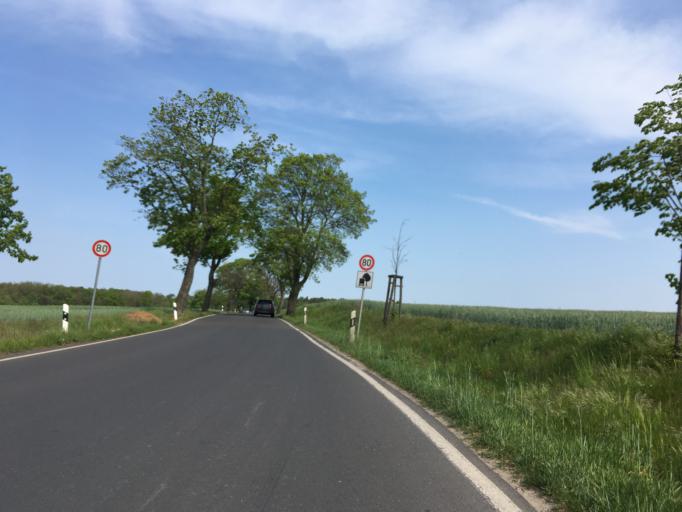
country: DE
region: Brandenburg
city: Werneuchen
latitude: 52.6078
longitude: 13.7577
